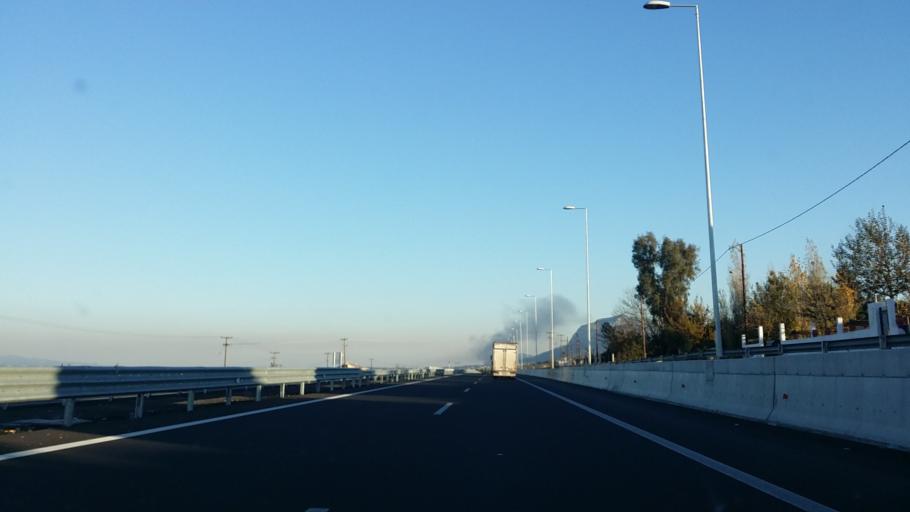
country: GR
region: Peloponnese
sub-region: Nomos Korinthias
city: Zevgolateio
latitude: 37.9250
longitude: 22.7997
